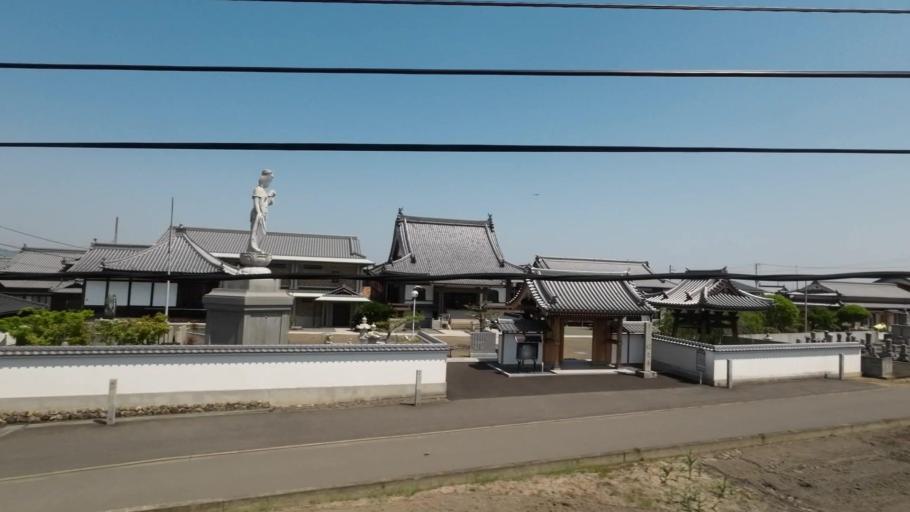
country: JP
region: Ehime
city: Saijo
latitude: 33.8983
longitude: 133.1071
